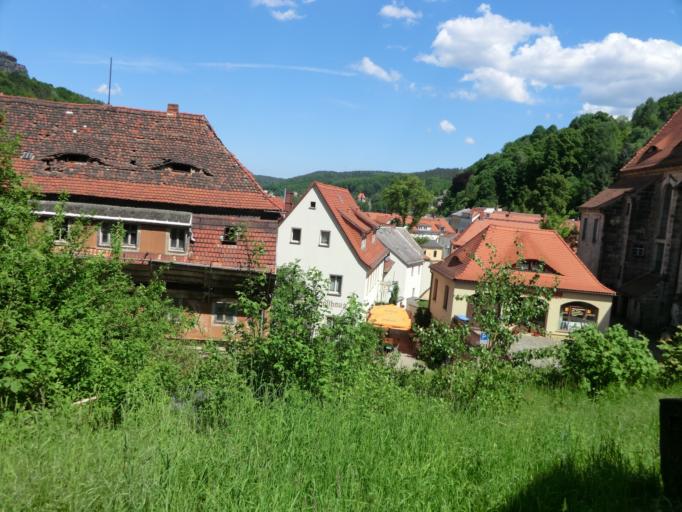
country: DE
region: Saxony
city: Konigstein
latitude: 50.9185
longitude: 14.0714
